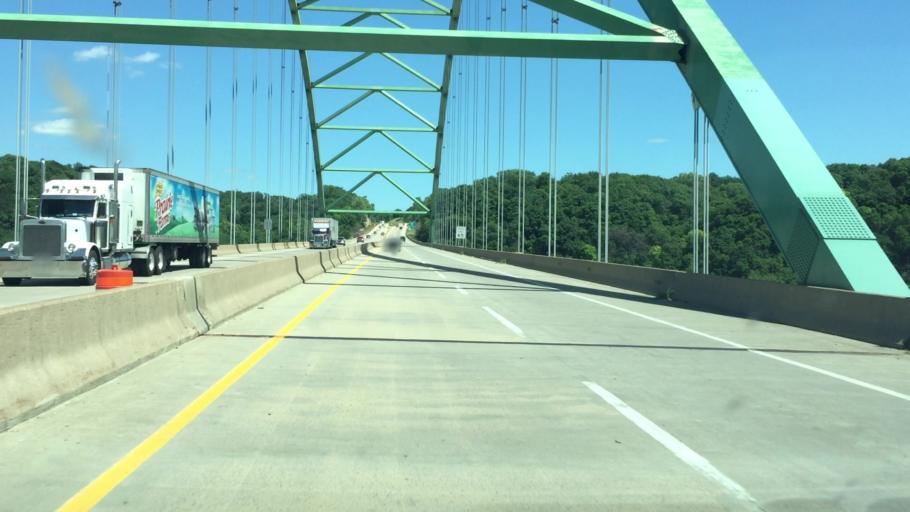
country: US
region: Illinois
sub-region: Jo Daviess County
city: East Dubuque
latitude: 42.5155
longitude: -90.6370
